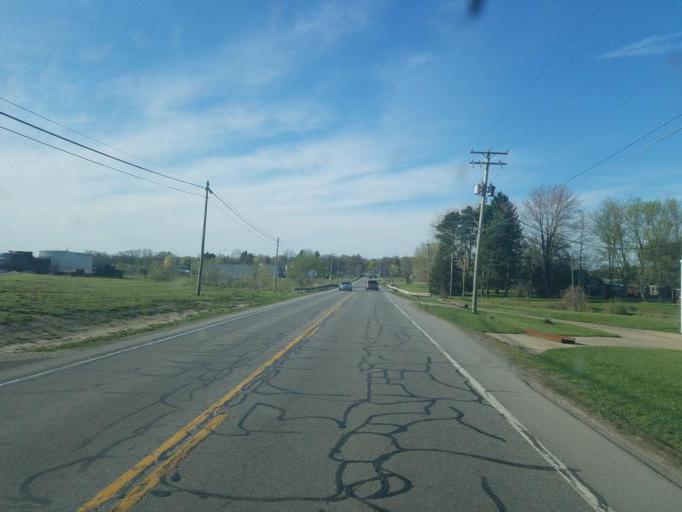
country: US
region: Ohio
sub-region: Ashland County
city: Ashland
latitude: 40.9553
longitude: -82.3643
